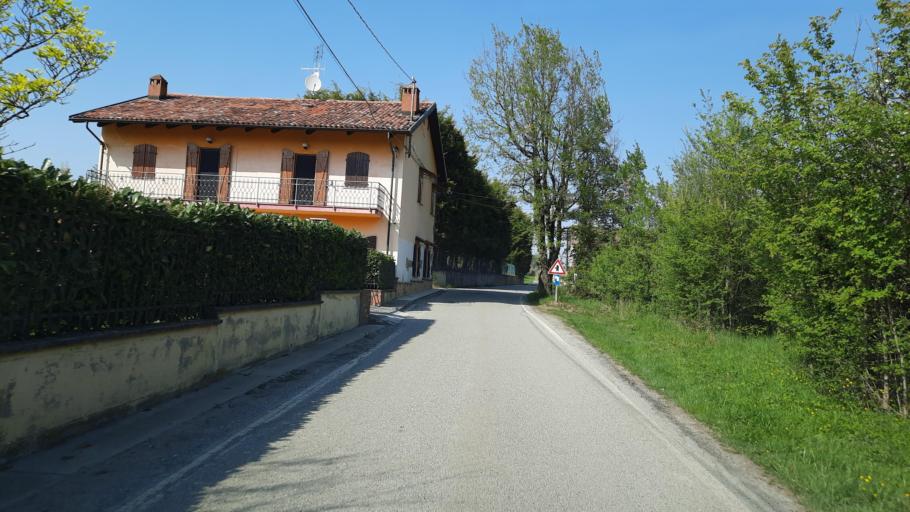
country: IT
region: Piedmont
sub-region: Provincia di Torino
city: Valentino
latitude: 45.1493
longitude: 8.0912
